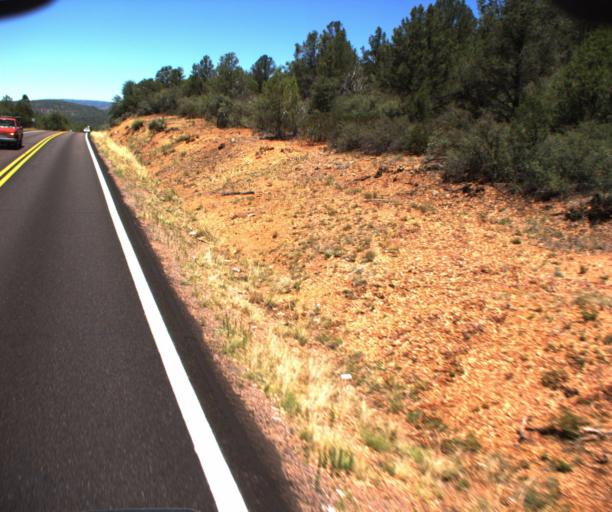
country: US
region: Arizona
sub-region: Gila County
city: Payson
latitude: 34.2882
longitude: -111.3422
